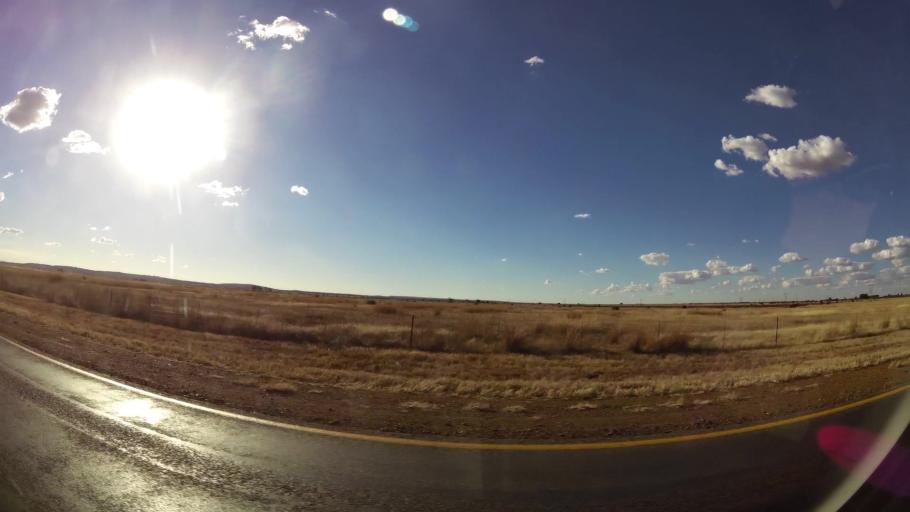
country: ZA
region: North-West
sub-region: Dr Kenneth Kaunda District Municipality
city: Stilfontein
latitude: -26.8434
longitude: 26.7376
